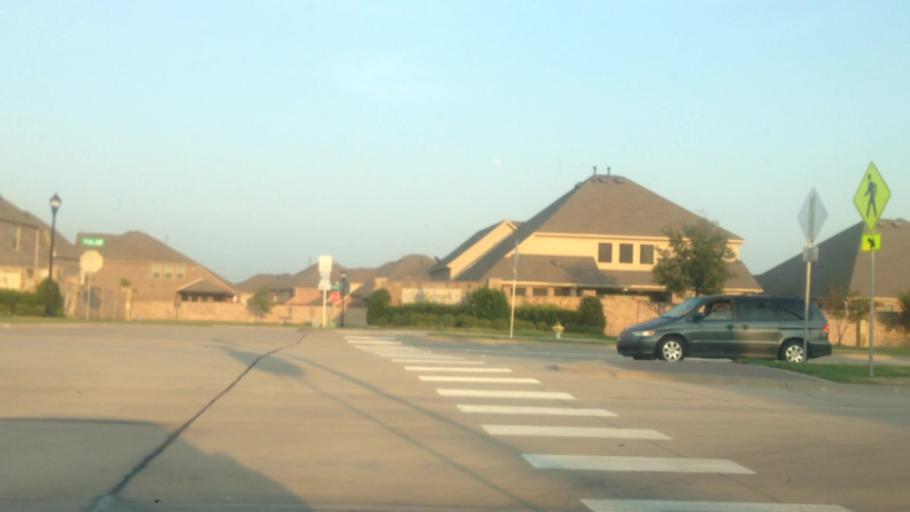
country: US
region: Texas
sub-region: Denton County
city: The Colony
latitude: 33.1228
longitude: -96.8721
